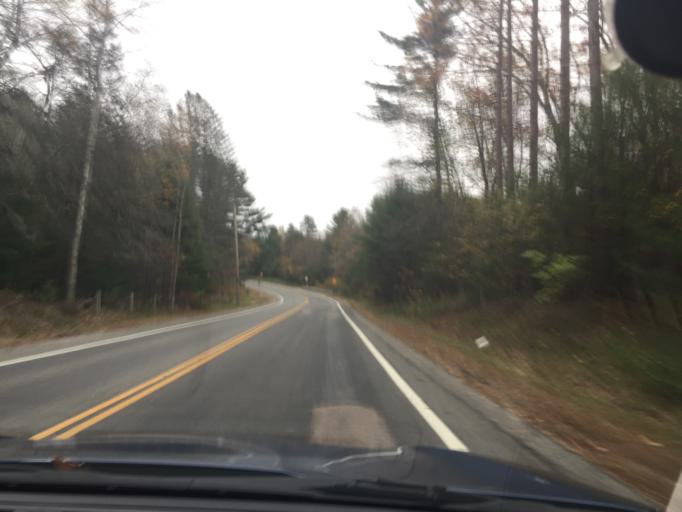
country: US
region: Rhode Island
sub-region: Providence County
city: North Scituate
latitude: 41.7907
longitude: -71.6077
